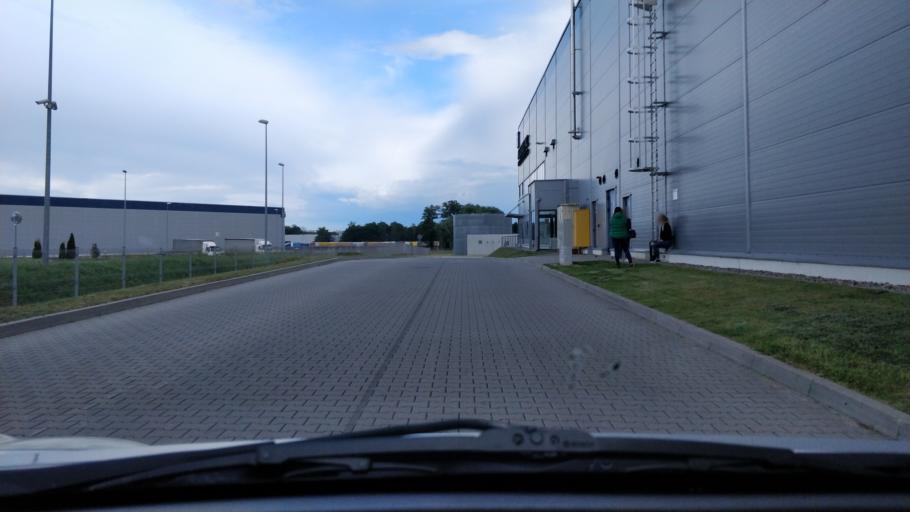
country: PL
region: Greater Poland Voivodeship
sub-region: Powiat poznanski
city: Daszewice
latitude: 52.3223
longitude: 17.0195
